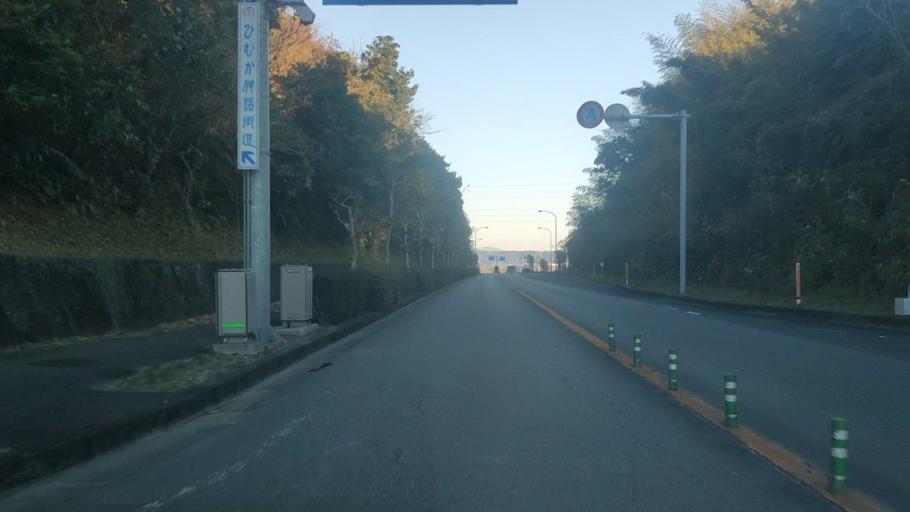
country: JP
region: Miyazaki
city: Tsuma
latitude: 32.0302
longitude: 131.4644
